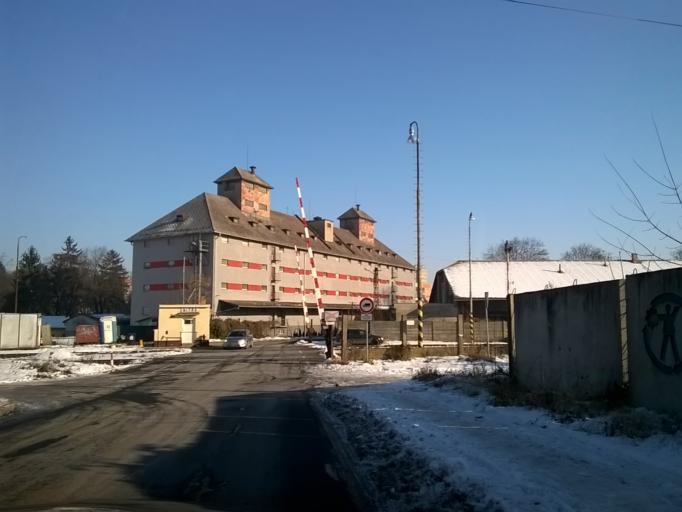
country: SK
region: Nitriansky
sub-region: Okres Nitra
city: Nitra
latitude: 48.3048
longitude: 18.0781
